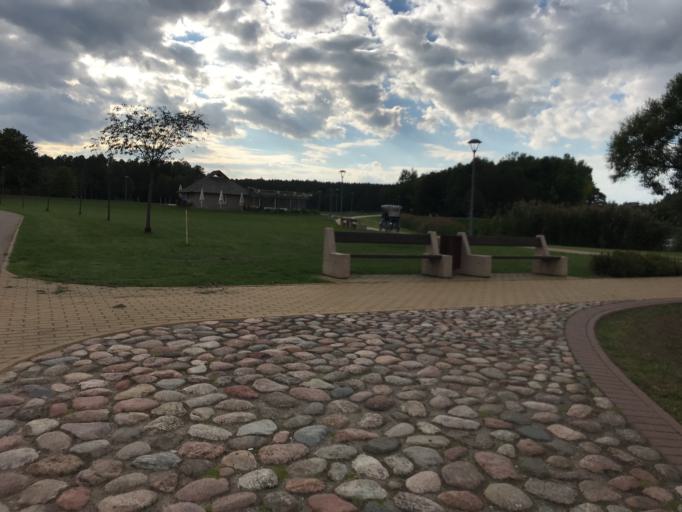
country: LT
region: Alytaus apskritis
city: Druskininkai
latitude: 54.0155
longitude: 23.9685
